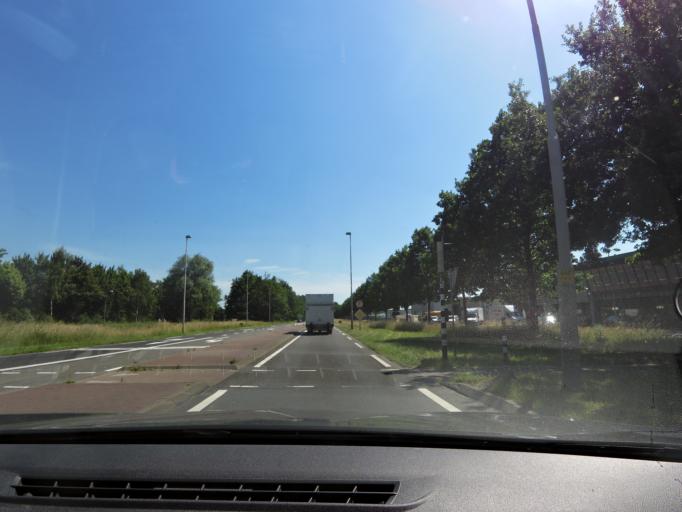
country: NL
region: Gelderland
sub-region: Berkelland
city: Eibergen
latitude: 52.0429
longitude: 6.6263
